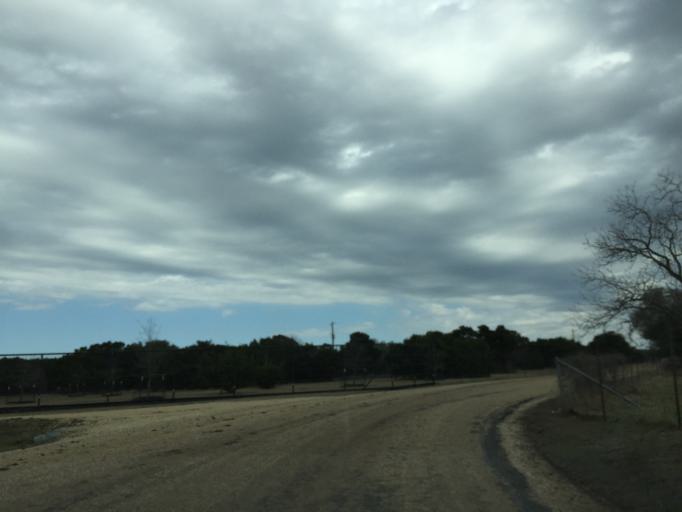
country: US
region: Texas
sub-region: Burnet County
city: Bertram
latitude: 30.6528
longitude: -98.0159
